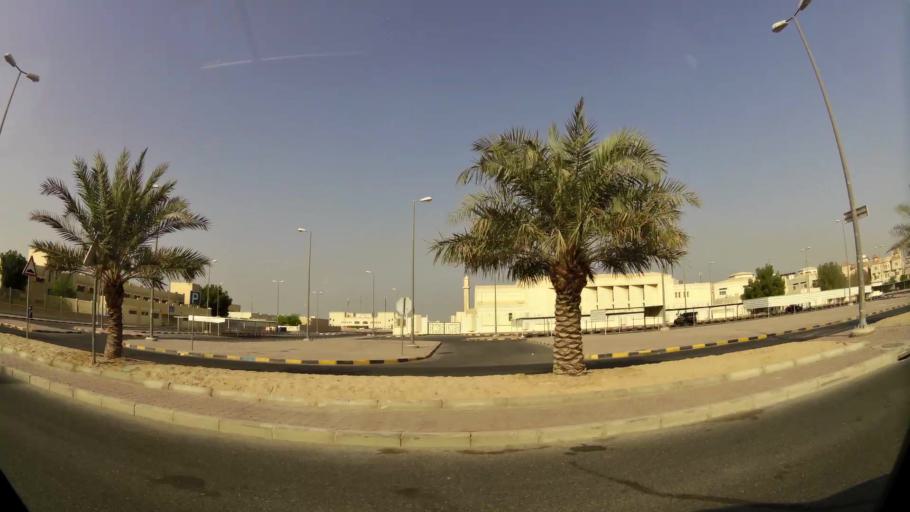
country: KW
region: Al Asimah
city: Ar Rabiyah
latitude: 29.2997
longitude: 47.7999
